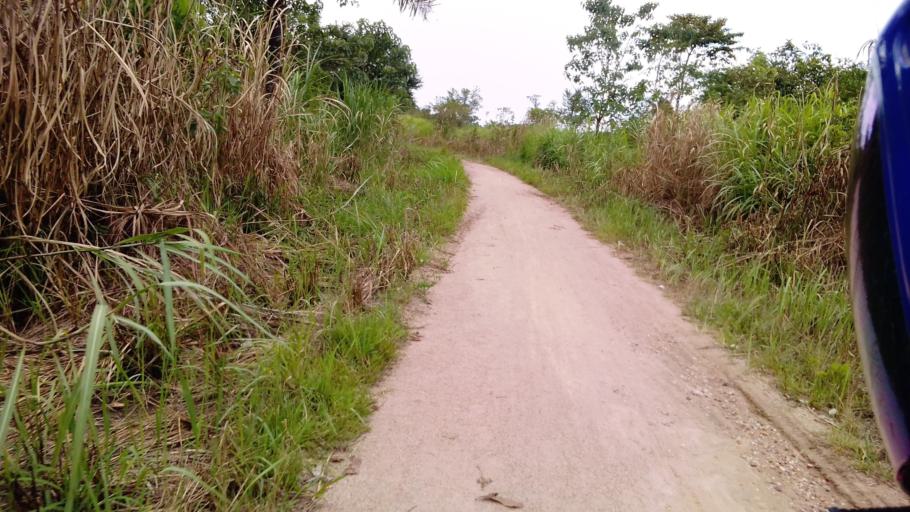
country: SL
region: Eastern Province
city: Koidu
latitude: 8.6754
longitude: -10.9858
